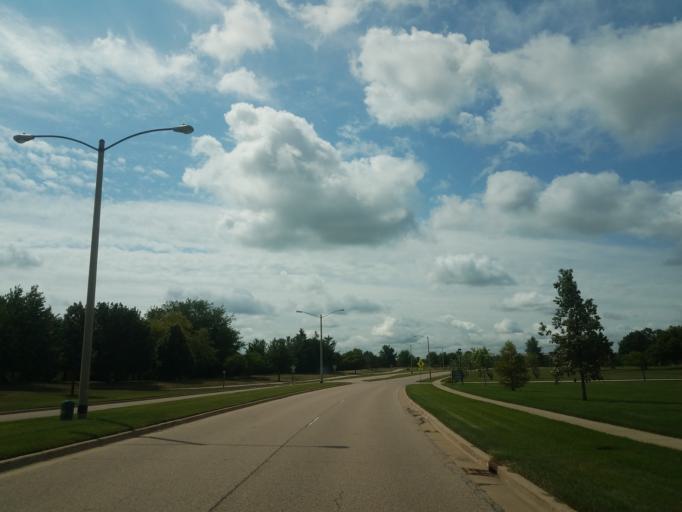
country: US
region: Illinois
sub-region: McLean County
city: Bloomington
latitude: 40.4643
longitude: -88.9500
